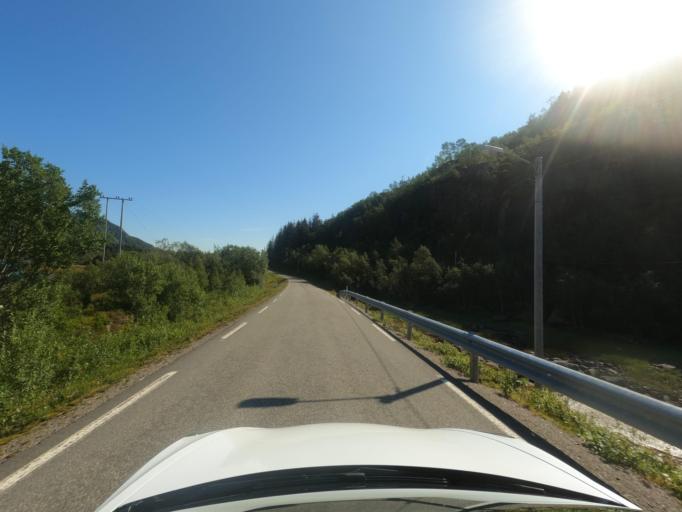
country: NO
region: Nordland
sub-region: Hadsel
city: Stokmarknes
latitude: 68.2990
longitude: 15.0412
